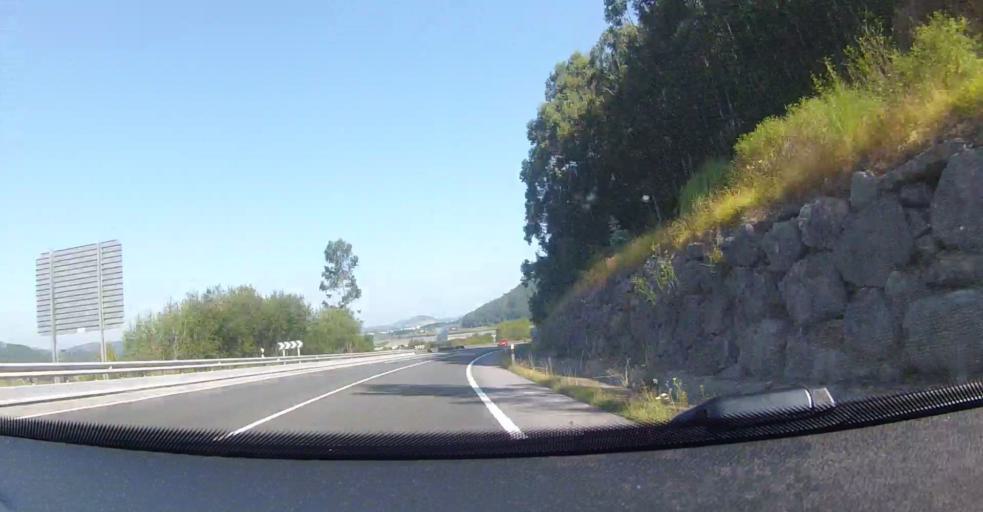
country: ES
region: Cantabria
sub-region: Provincia de Cantabria
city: Limpias
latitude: 43.3691
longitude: -3.4266
